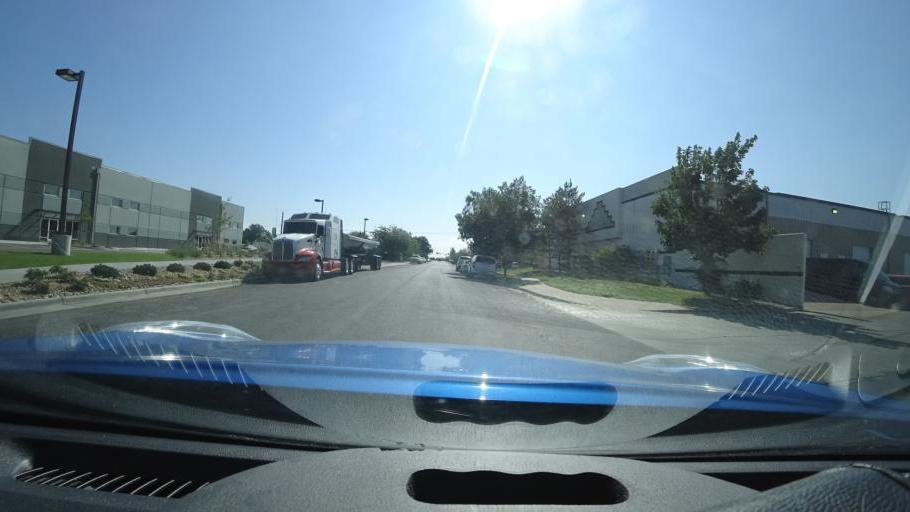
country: US
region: Colorado
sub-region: Adams County
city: Aurora
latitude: 39.7193
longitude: -104.7945
